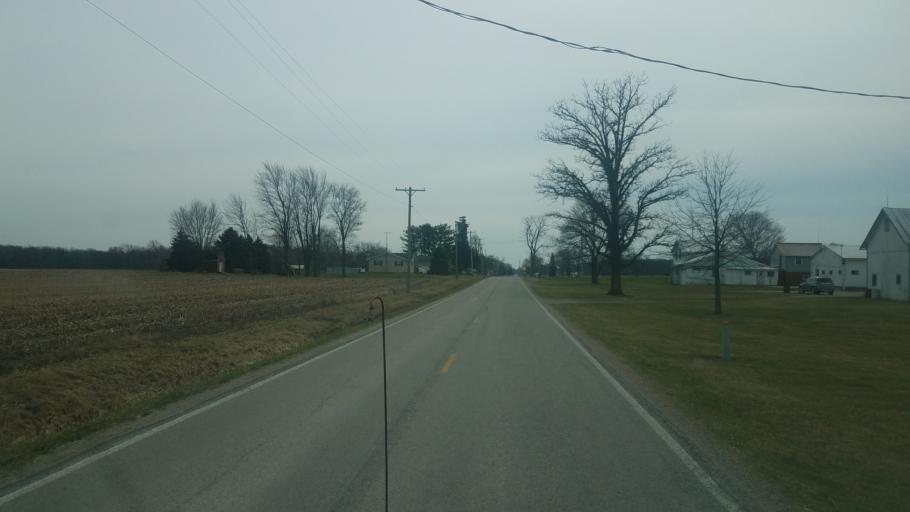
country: US
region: Ohio
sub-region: Huron County
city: Wakeman
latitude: 41.1793
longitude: -82.4903
